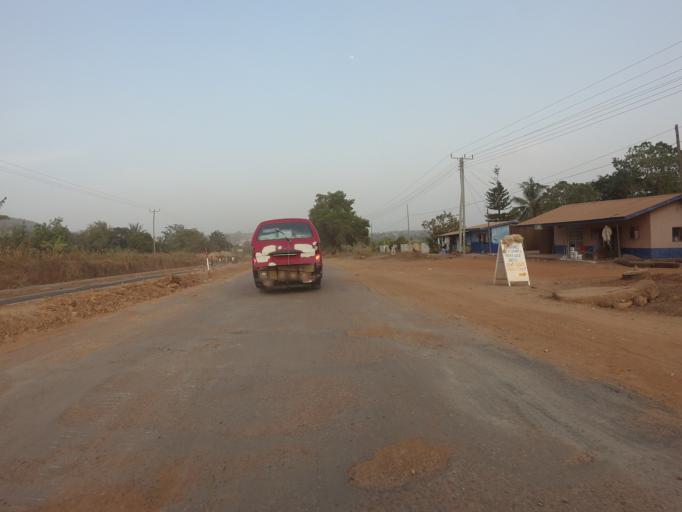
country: GH
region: Volta
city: Ho
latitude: 6.5937
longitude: 0.4379
